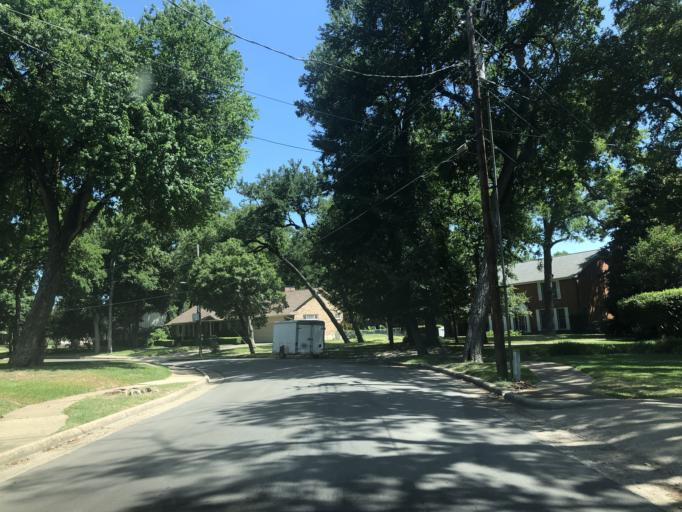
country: US
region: Texas
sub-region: Dallas County
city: Duncanville
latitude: 32.6498
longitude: -96.9196
